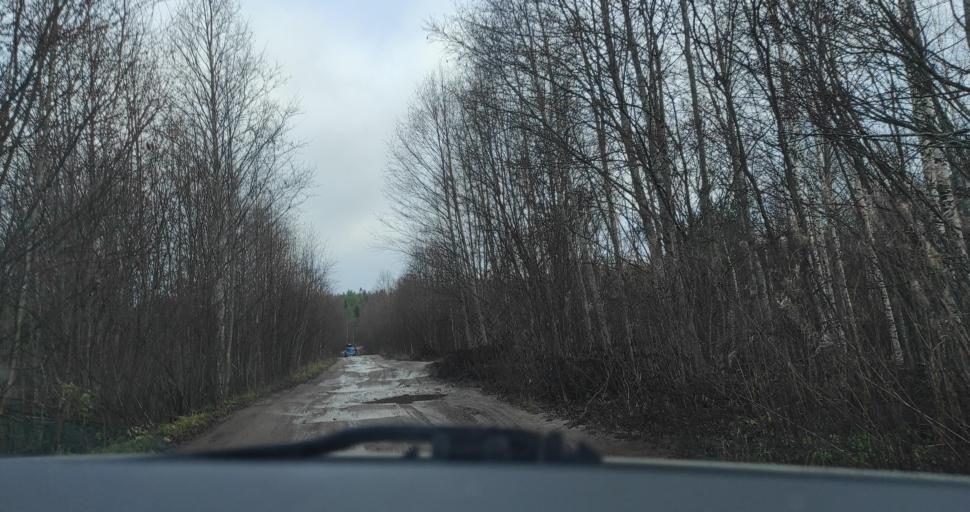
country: RU
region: Republic of Karelia
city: Pitkyaranta
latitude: 61.7341
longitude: 31.3862
